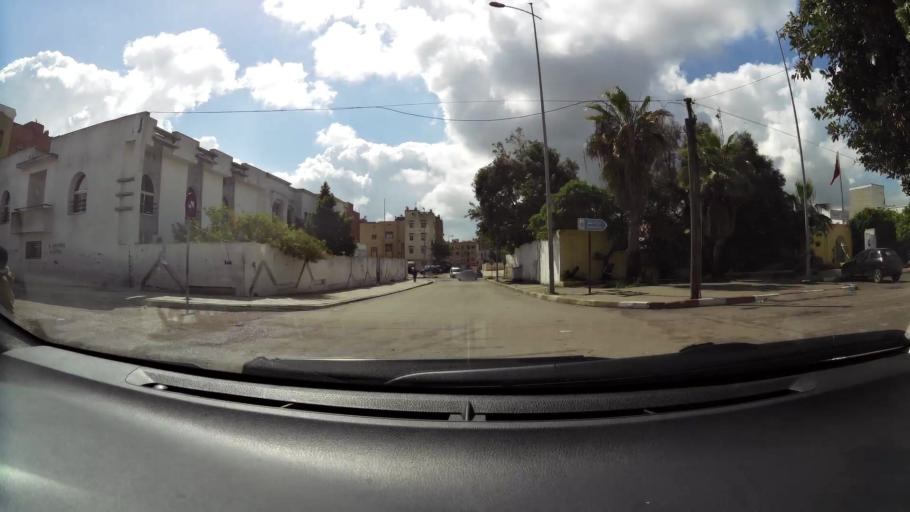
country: MA
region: Grand Casablanca
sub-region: Mediouna
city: Tit Mellil
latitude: 33.5496
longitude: -7.4863
